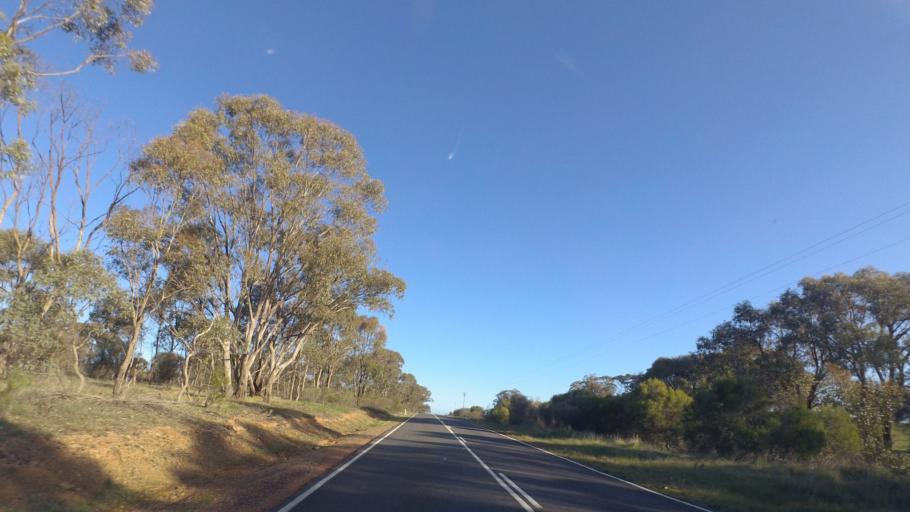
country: AU
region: Victoria
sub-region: Greater Bendigo
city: Kennington
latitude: -36.8636
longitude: 144.5021
